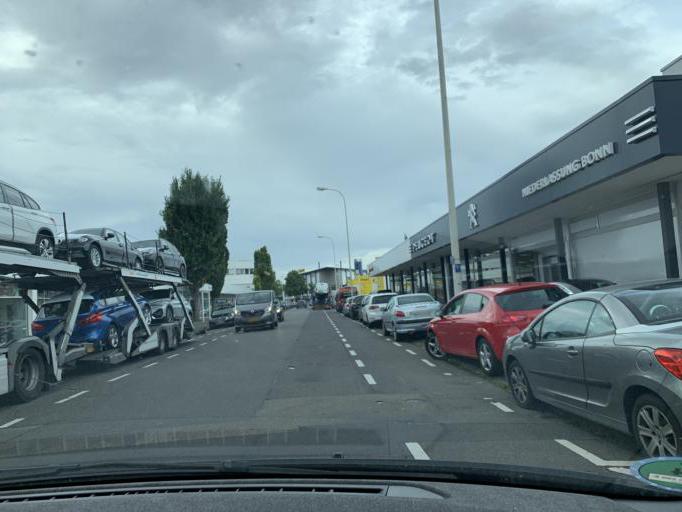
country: DE
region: North Rhine-Westphalia
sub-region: Regierungsbezirk Koln
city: Bonn
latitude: 50.7407
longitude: 7.0819
